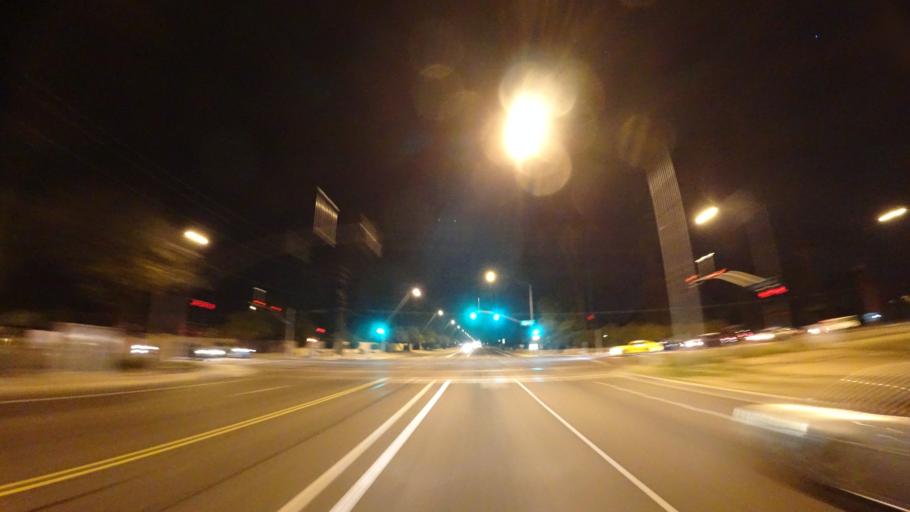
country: US
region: Arizona
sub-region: Maricopa County
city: Mesa
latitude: 33.4370
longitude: -111.8058
